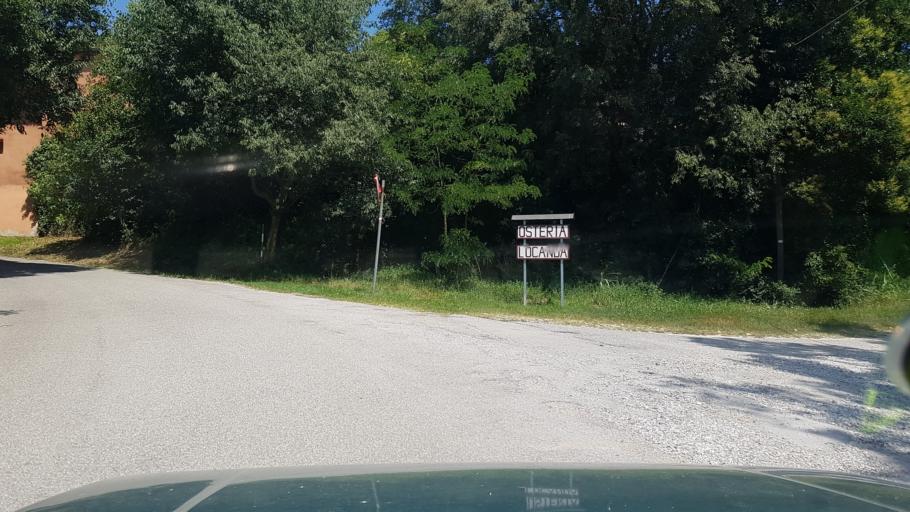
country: IT
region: Friuli Venezia Giulia
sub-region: Provincia di Gorizia
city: Farra d'Isonzo
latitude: 45.9052
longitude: 13.5411
